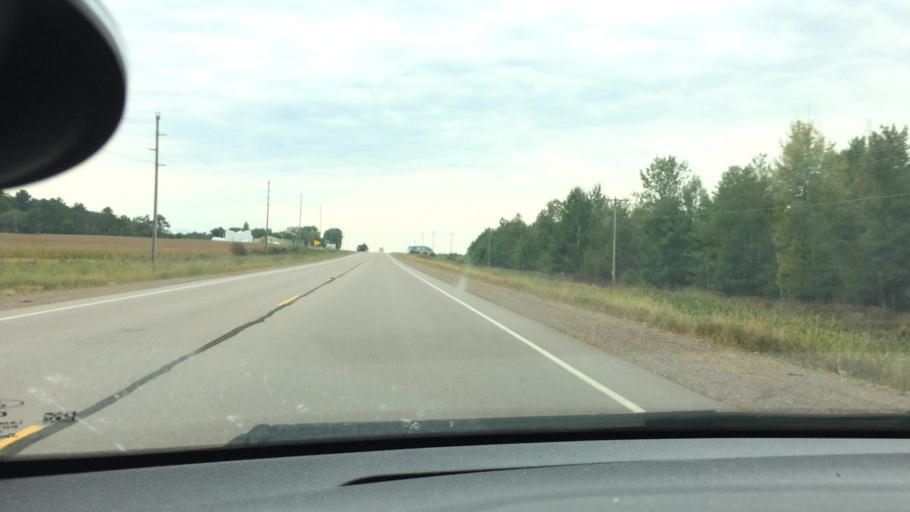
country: US
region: Wisconsin
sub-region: Eau Claire County
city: Augusta
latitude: 44.5964
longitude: -90.9280
